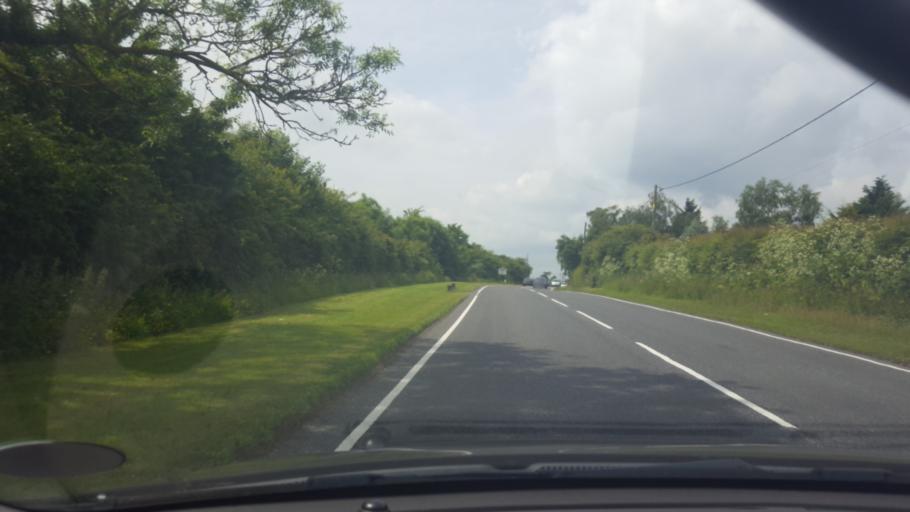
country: GB
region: England
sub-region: Essex
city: Little Clacton
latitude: 51.8601
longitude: 1.1275
